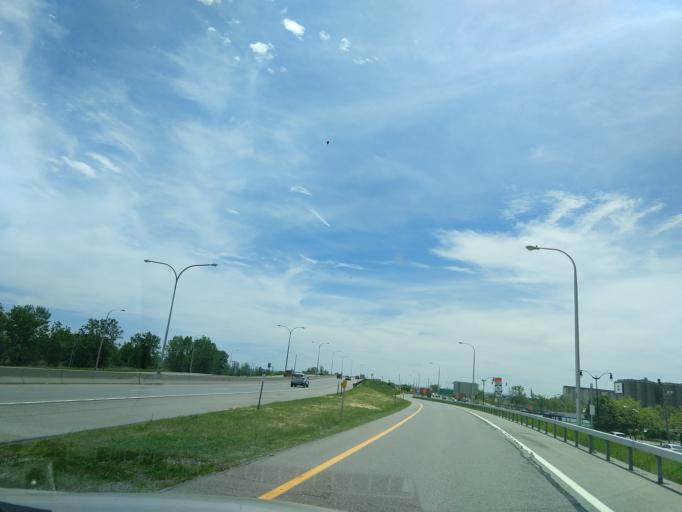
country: US
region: New York
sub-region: Erie County
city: Lackawanna
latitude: 42.8419
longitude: -78.8587
